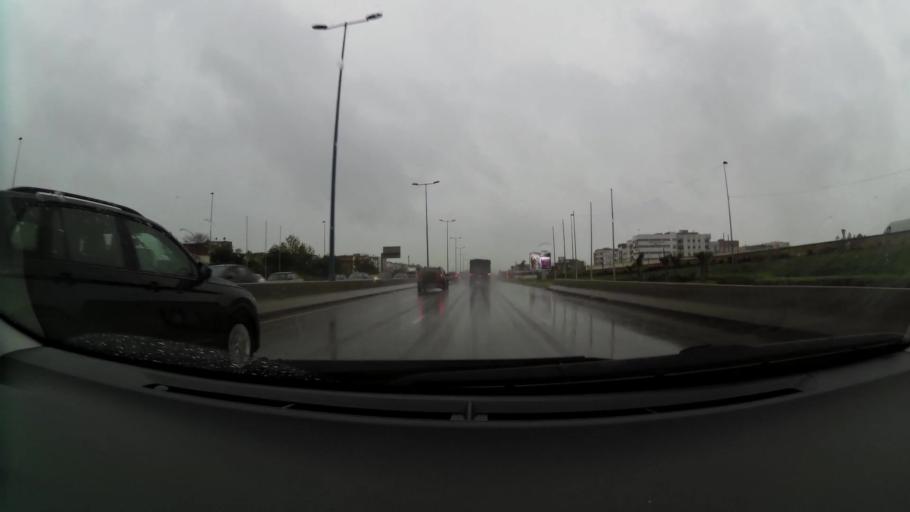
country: MA
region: Grand Casablanca
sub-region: Mediouna
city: Tit Mellil
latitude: 33.5838
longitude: -7.5459
